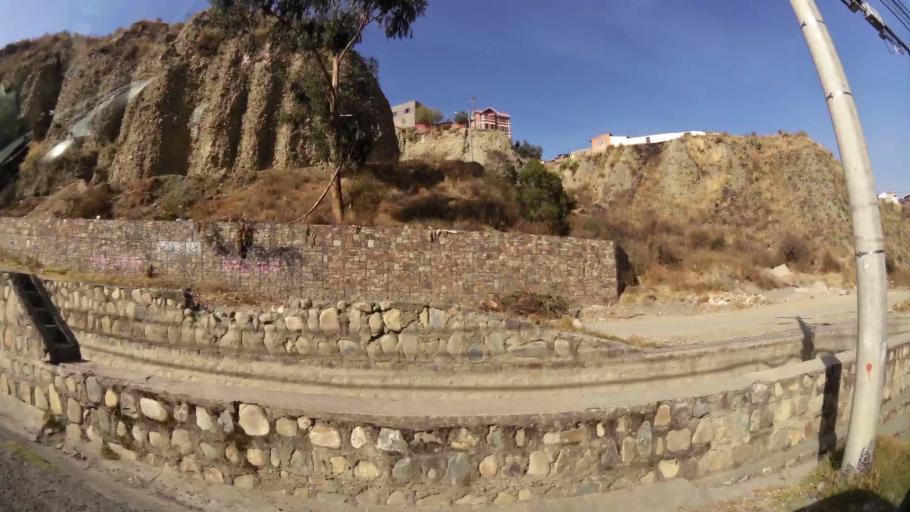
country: BO
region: La Paz
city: La Paz
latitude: -16.5262
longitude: -68.0786
